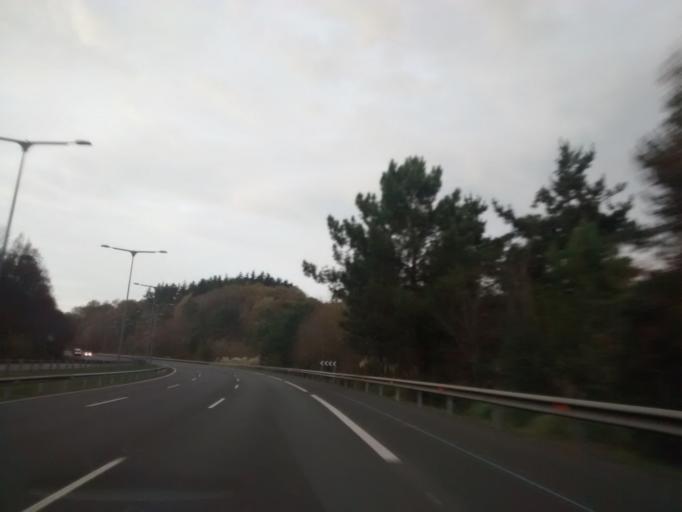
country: ES
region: Basque Country
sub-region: Bizkaia
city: Arrigorriaga
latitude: 43.2149
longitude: -2.8970
